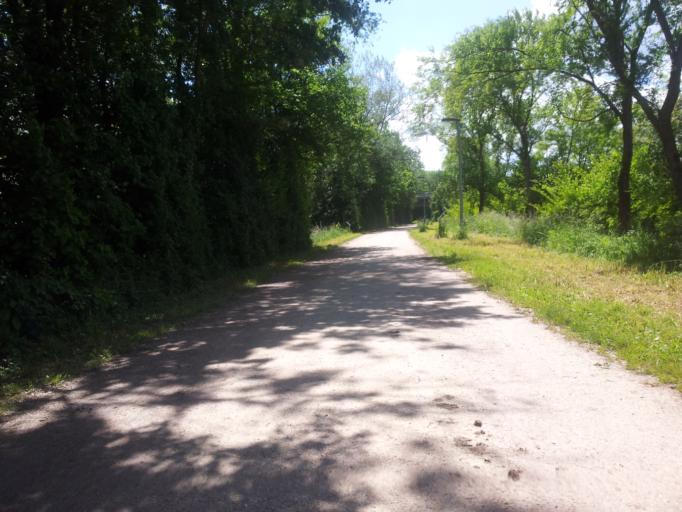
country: DE
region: Baden-Wuerttemberg
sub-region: Regierungsbezirk Stuttgart
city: Kongen
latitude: 48.6844
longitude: 9.3788
